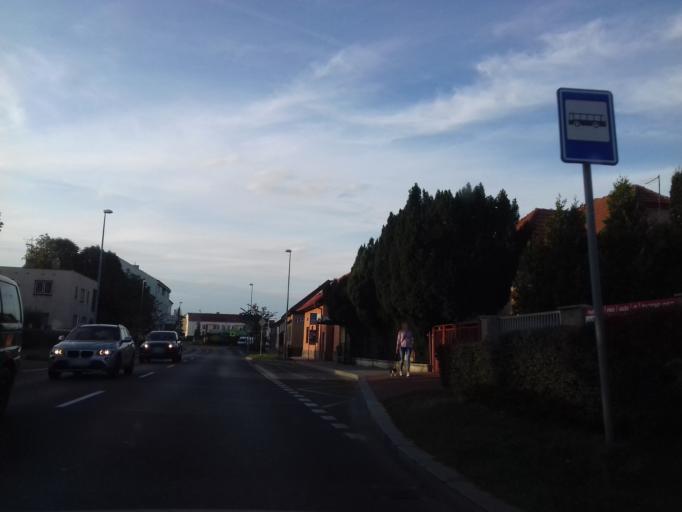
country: CZ
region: Praha
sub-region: Praha 4
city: Hodkovicky
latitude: 50.0129
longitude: 14.4581
